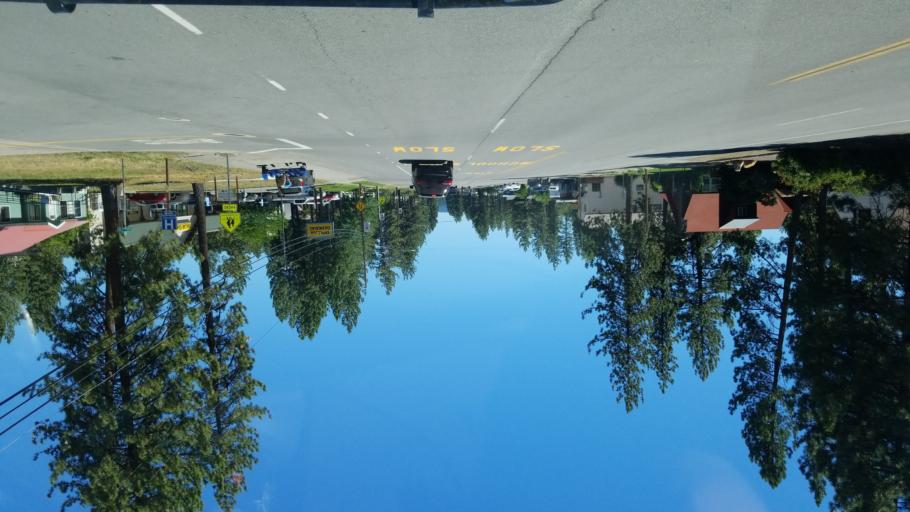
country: US
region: California
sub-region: Plumas County
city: Chester
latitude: 40.3045
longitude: -121.2335
